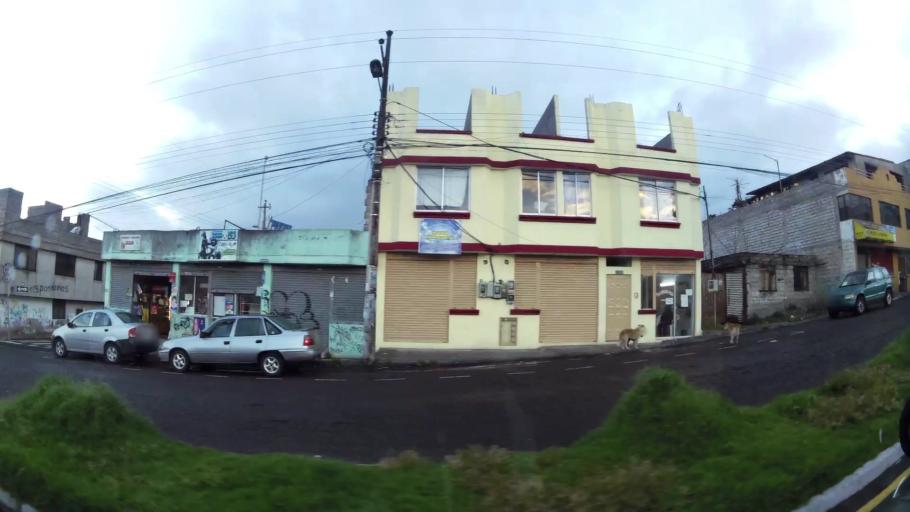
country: EC
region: Pichincha
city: Quito
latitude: -0.0903
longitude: -78.5199
